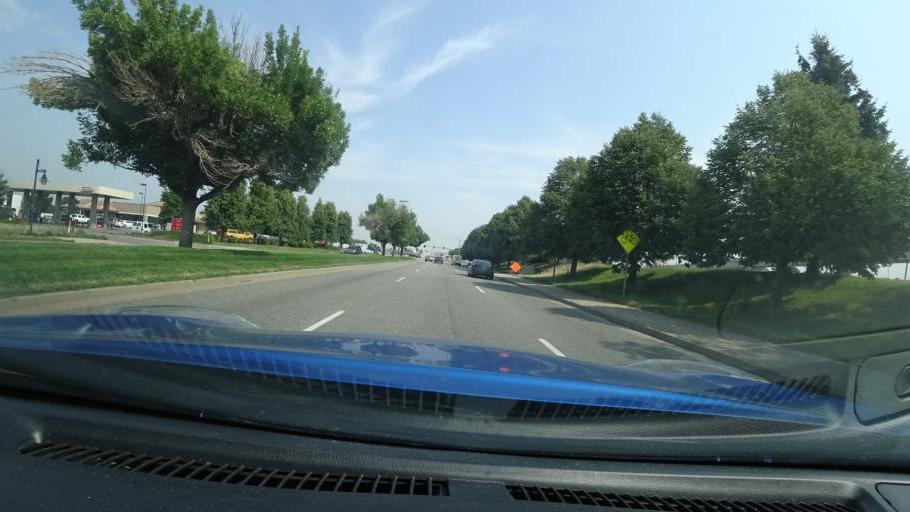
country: US
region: Colorado
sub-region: Adams County
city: Aurora
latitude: 39.7603
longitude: -104.7911
